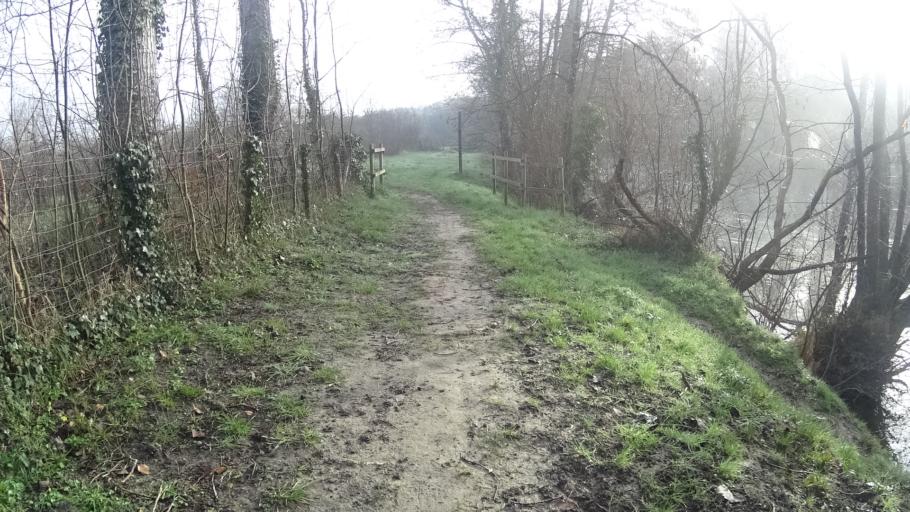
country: FR
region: Poitou-Charentes
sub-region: Departement de la Charente-Maritime
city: Saint-Aigulin
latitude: 45.1509
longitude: -0.0028
